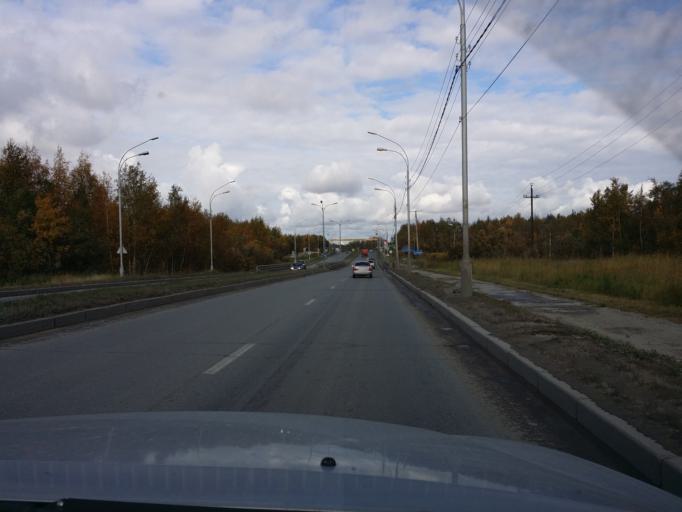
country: RU
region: Khanty-Mansiyskiy Avtonomnyy Okrug
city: Nizhnevartovsk
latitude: 60.9711
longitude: 76.5275
